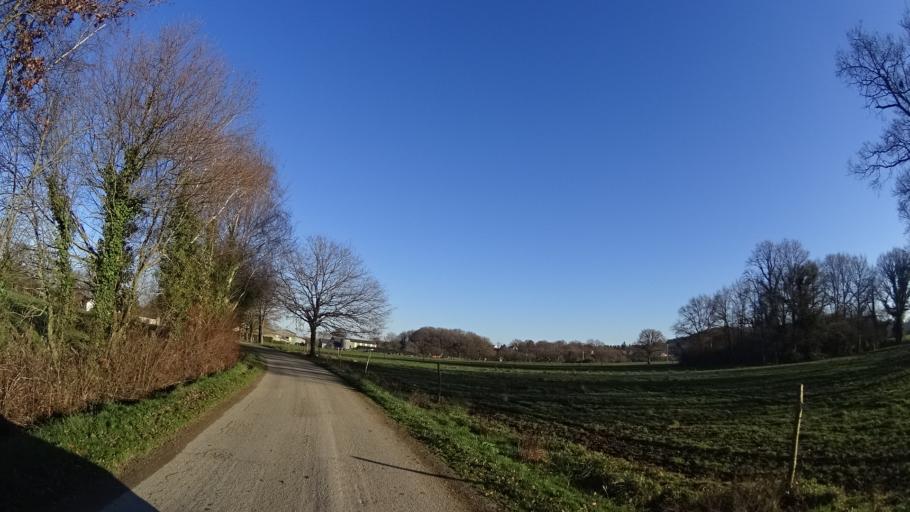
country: FR
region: Brittany
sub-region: Departement du Morbihan
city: Allaire
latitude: 47.6701
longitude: -2.1641
